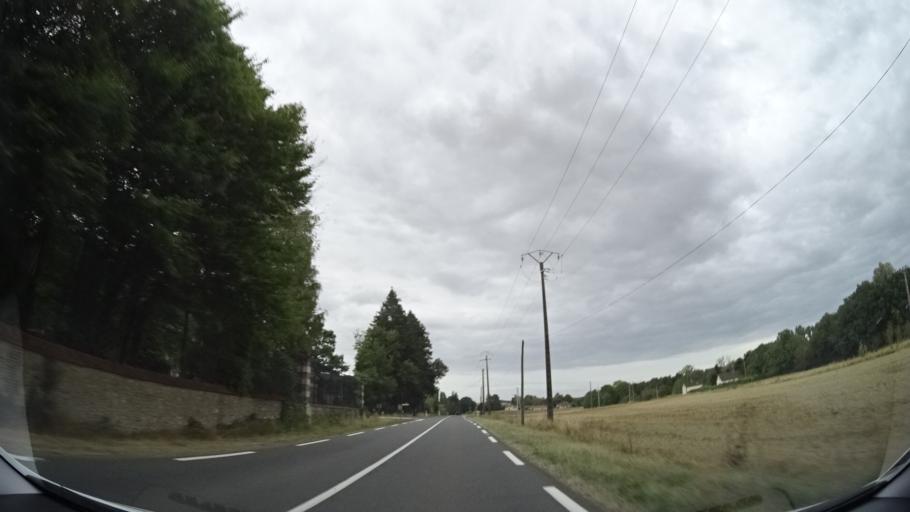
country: FR
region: Centre
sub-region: Departement du Loiret
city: Douchy
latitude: 47.9454
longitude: 3.0371
